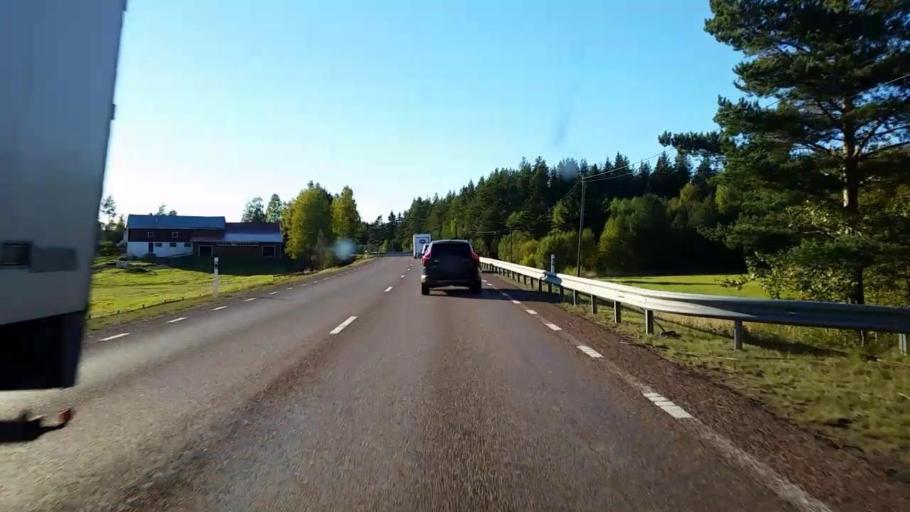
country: SE
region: Gaevleborg
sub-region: Ljusdals Kommun
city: Jaervsoe
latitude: 61.8043
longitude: 16.2930
